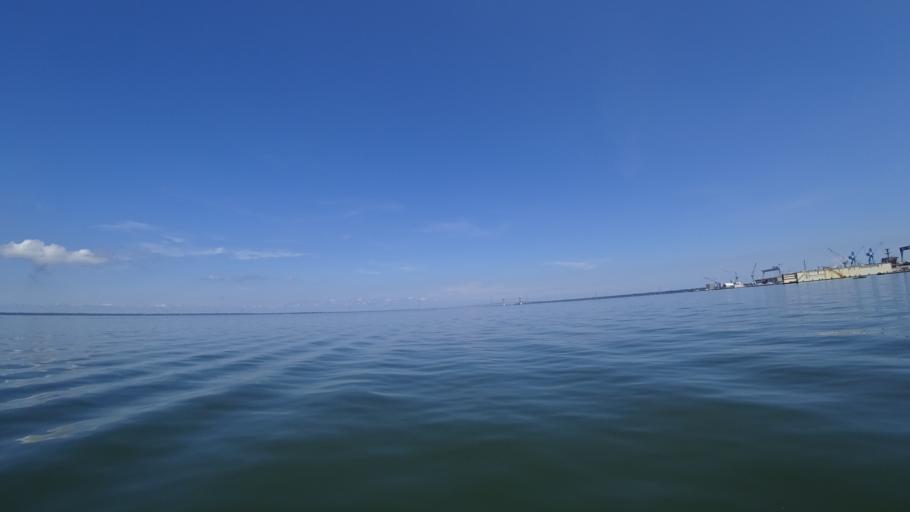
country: US
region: Virginia
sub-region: City of Newport News
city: Newport News
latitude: 36.9814
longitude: -76.4482
